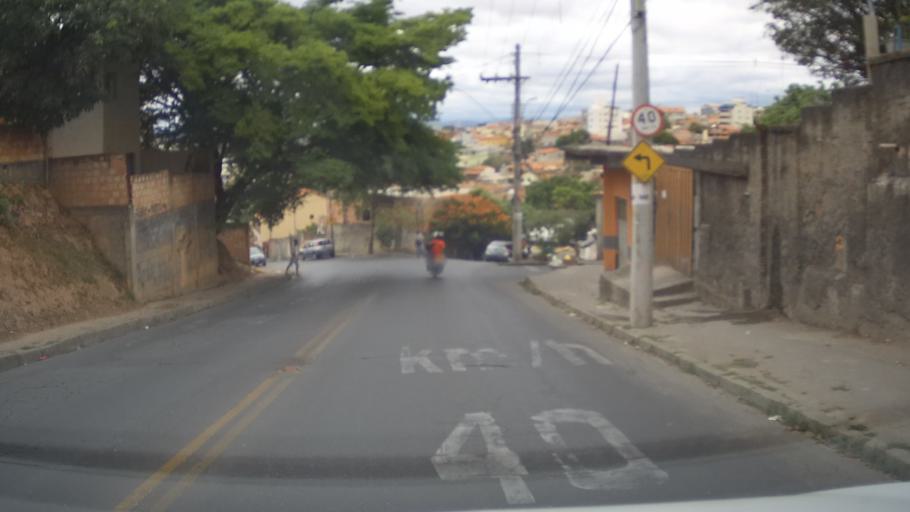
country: BR
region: Minas Gerais
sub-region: Belo Horizonte
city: Belo Horizonte
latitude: -19.8396
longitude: -43.9274
